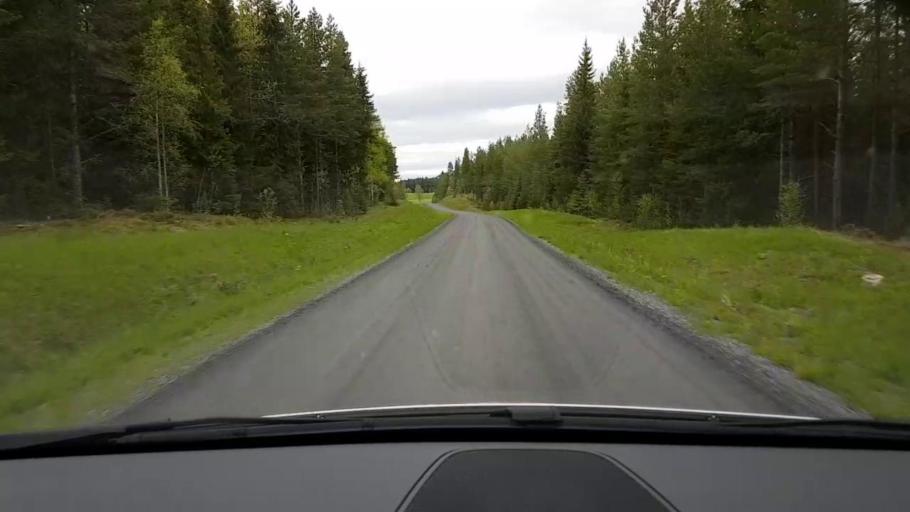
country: SE
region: Jaemtland
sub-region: Krokoms Kommun
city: Krokom
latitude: 63.3038
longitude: 14.3967
